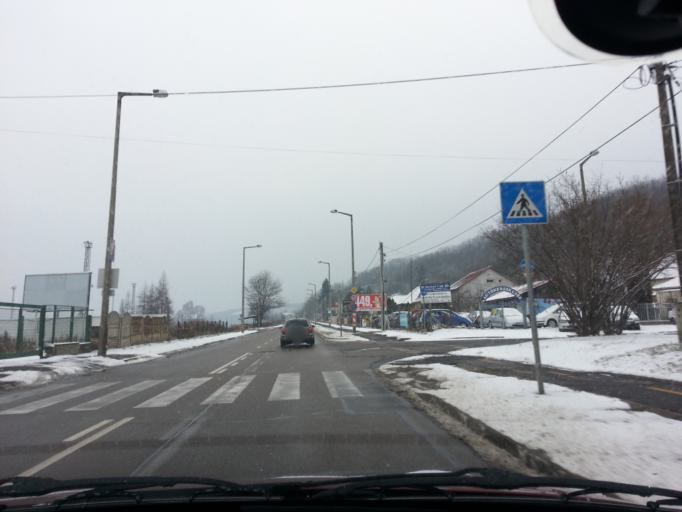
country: HU
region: Nograd
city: Salgotarjan
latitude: 48.0944
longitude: 19.7949
